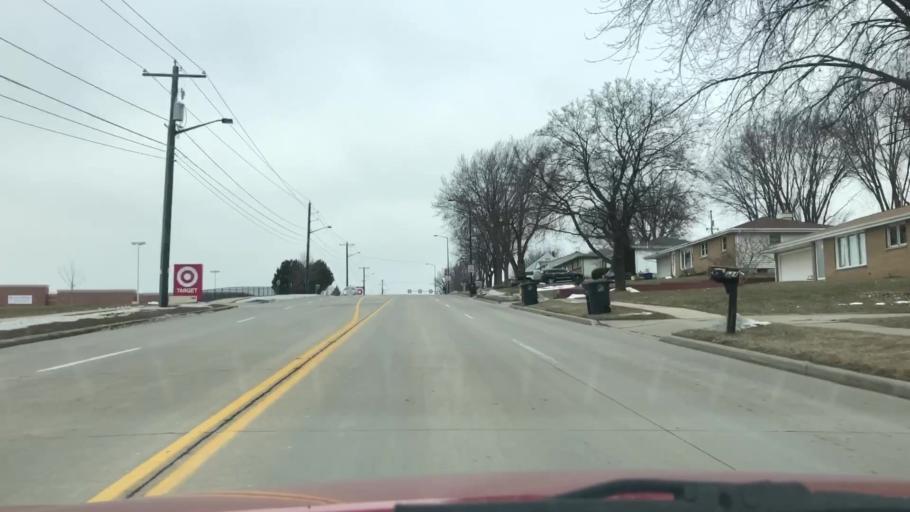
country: US
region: Wisconsin
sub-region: Brown County
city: Ashwaubenon
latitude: 44.4905
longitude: -88.0681
